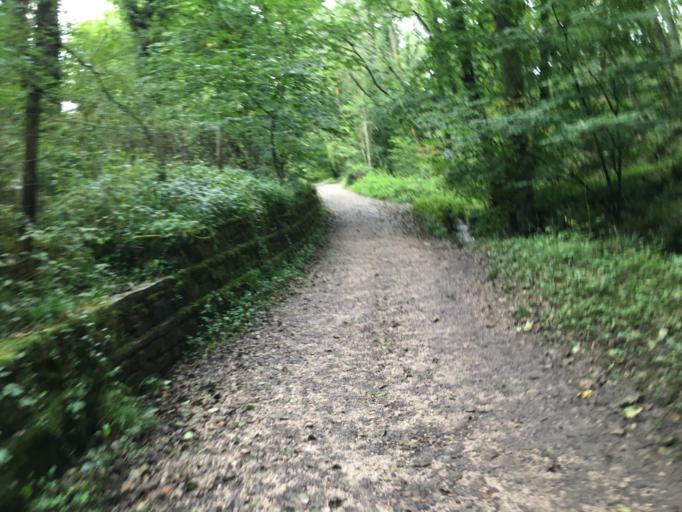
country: GB
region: England
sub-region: North Yorkshire
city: Sleights
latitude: 54.4050
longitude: -0.7280
